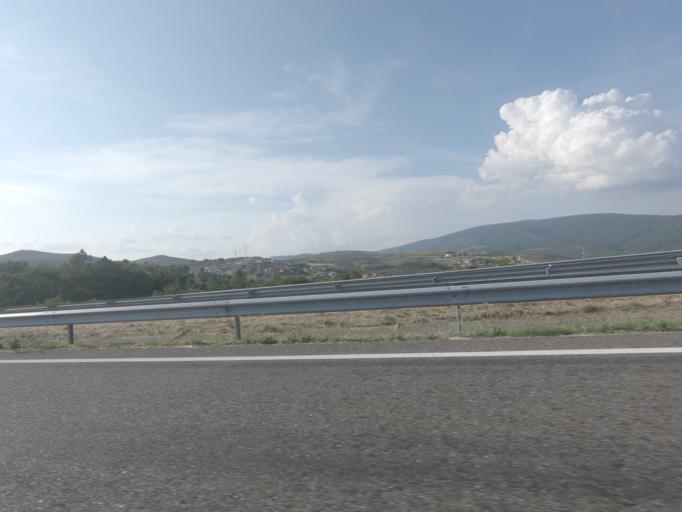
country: ES
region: Galicia
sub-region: Provincia de Ourense
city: Cualedro
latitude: 41.9646
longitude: -7.5236
